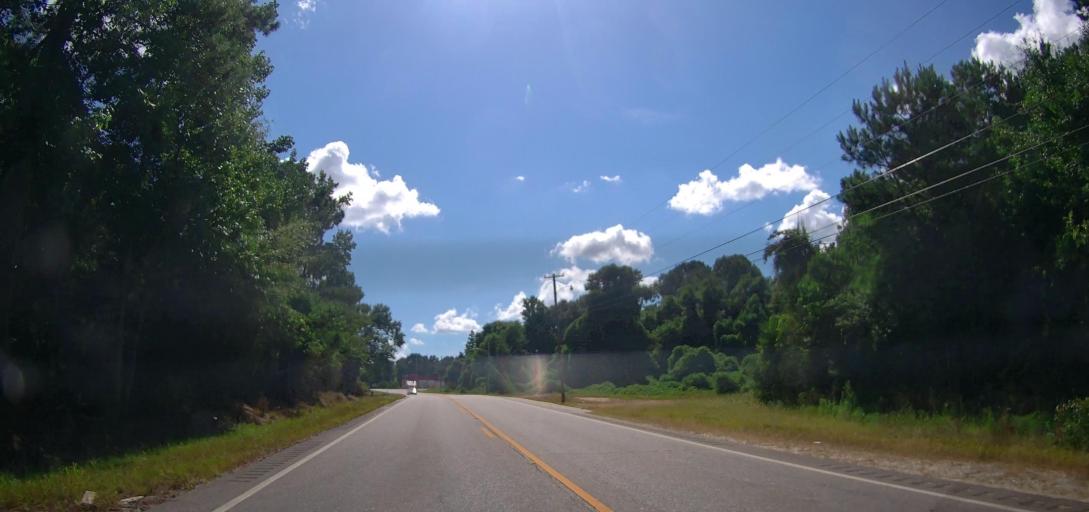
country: US
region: Alabama
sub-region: Macon County
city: Tuskegee
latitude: 32.4405
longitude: -85.6638
